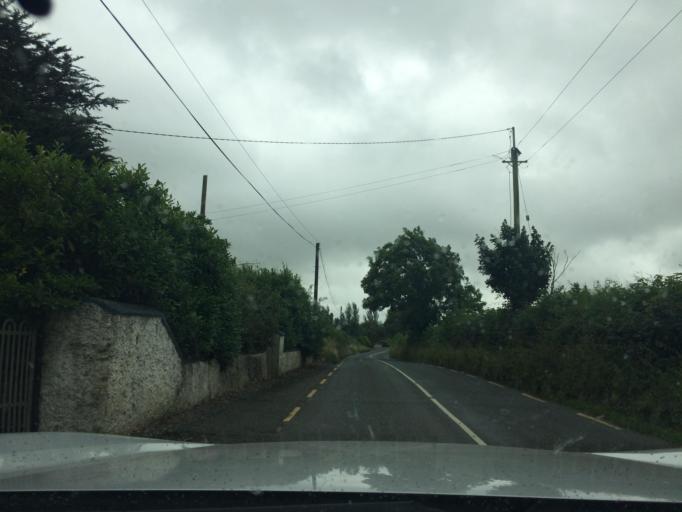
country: IE
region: Munster
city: Cashel
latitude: 52.5408
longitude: -7.8926
